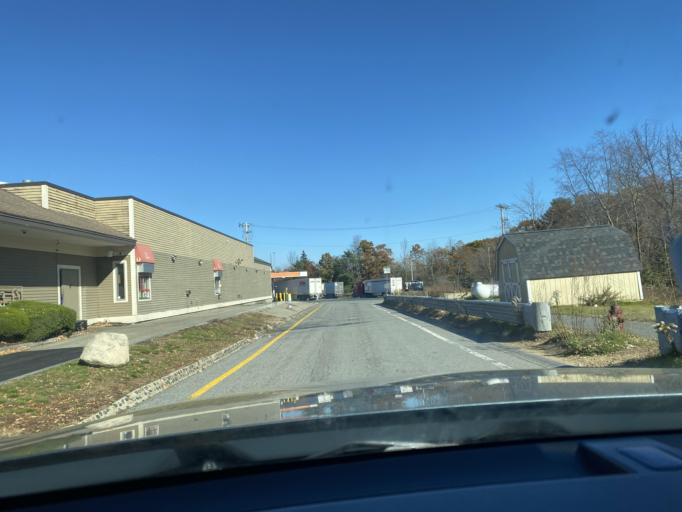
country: US
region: Massachusetts
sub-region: Worcester County
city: Charlton
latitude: 42.1394
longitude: -72.0250
